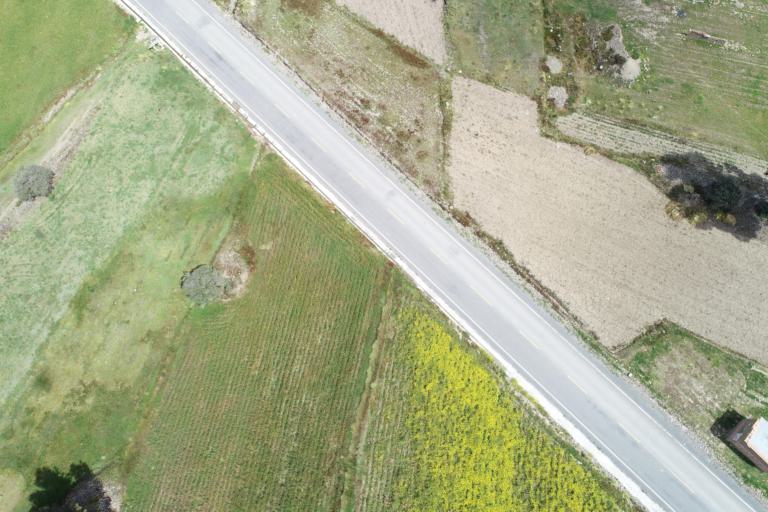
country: BO
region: La Paz
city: Achacachi
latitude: -16.0228
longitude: -68.6191
